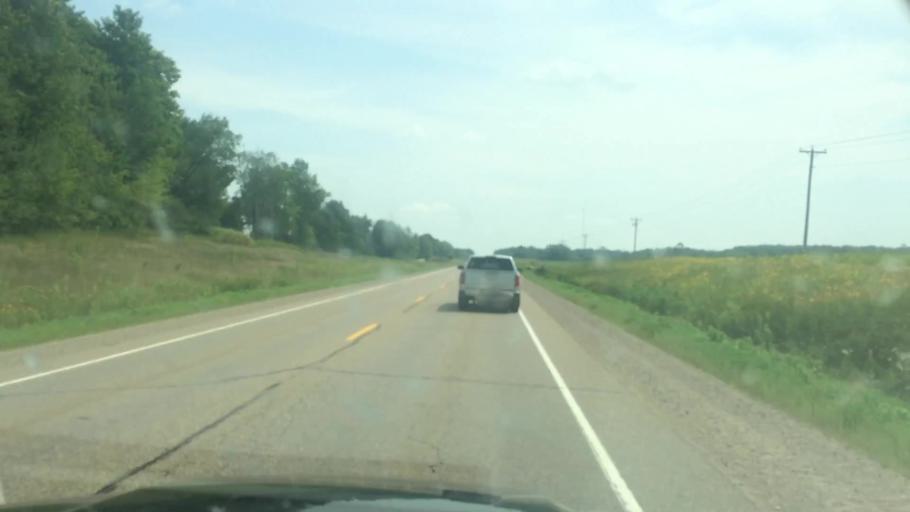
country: US
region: Wisconsin
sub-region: Langlade County
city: Antigo
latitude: 45.1681
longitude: -88.9158
